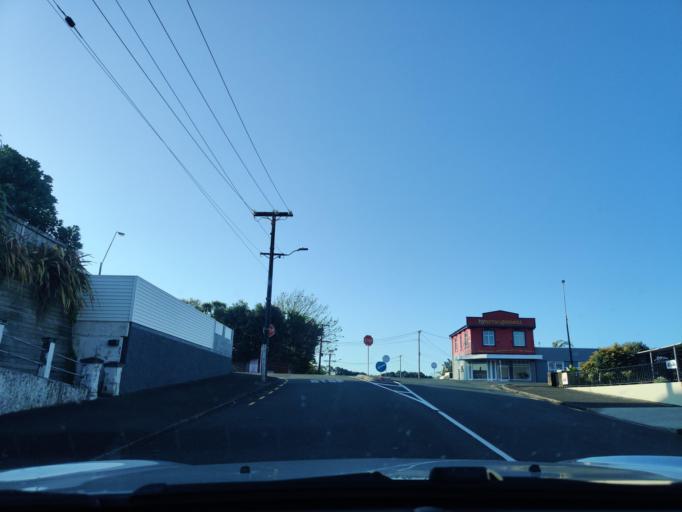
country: NZ
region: Taranaki
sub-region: New Plymouth District
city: New Plymouth
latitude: -39.0590
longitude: 174.0620
